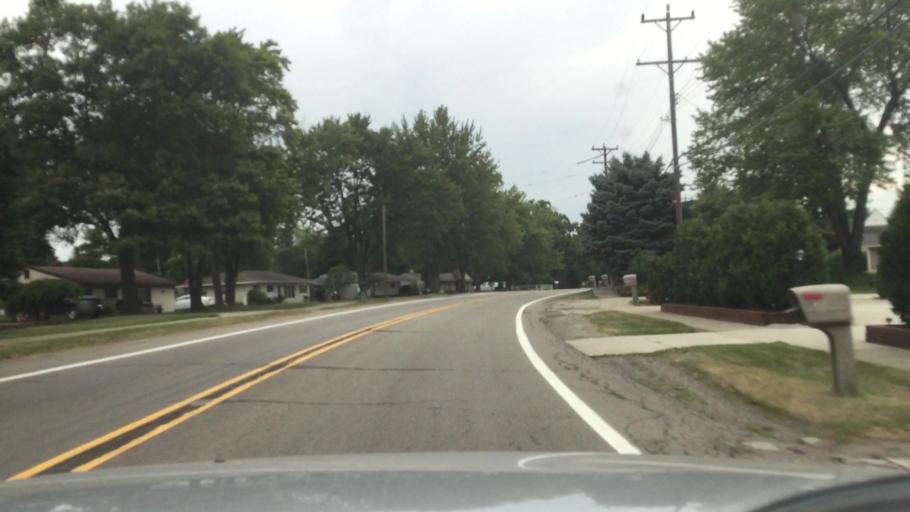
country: US
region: Michigan
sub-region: Oakland County
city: Waterford
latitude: 42.6823
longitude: -83.4235
